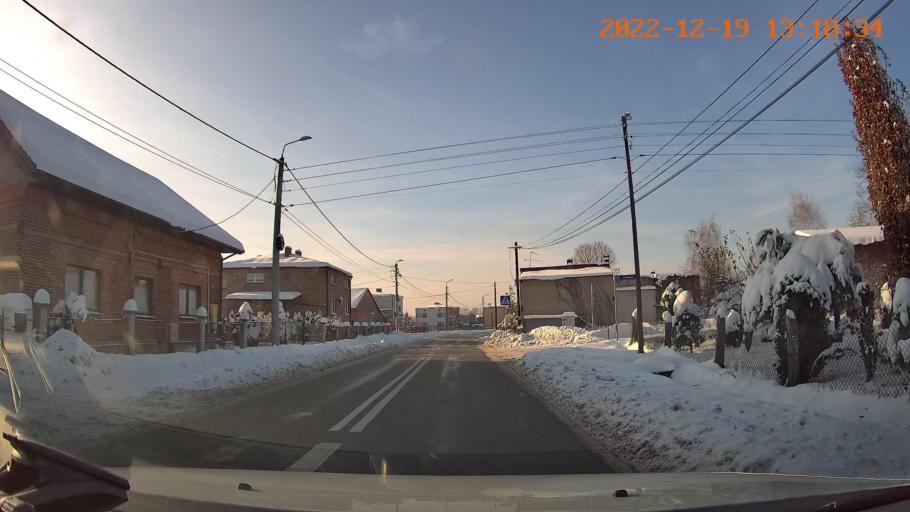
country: PL
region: Silesian Voivodeship
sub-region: Powiat bierunsko-ledzinski
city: Chelm Slaski
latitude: 50.1065
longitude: 19.1971
